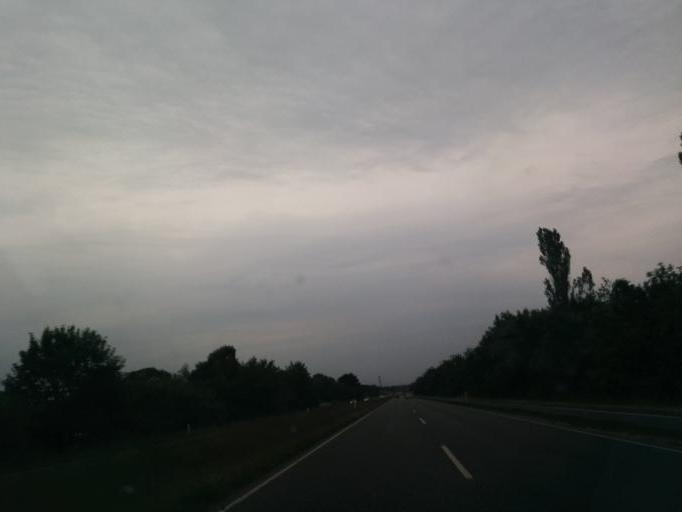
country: DK
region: Central Jutland
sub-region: Arhus Kommune
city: Hjortshoj
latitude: 56.2404
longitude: 10.2989
